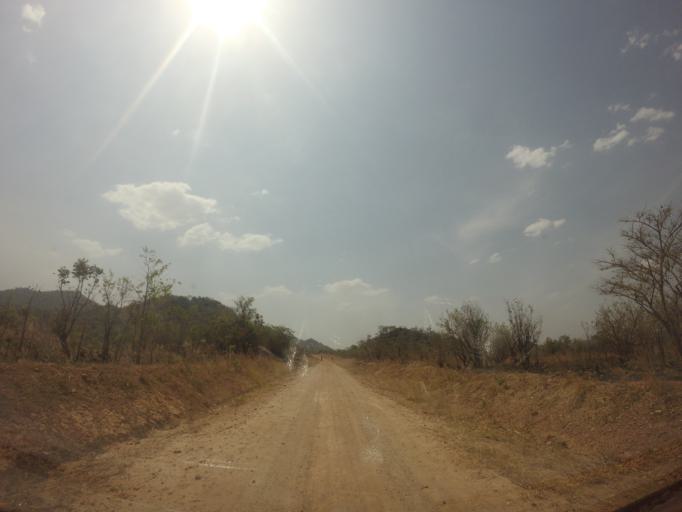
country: UG
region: Northern Region
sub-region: Arua District
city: Arua
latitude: 2.8972
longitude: 31.1085
